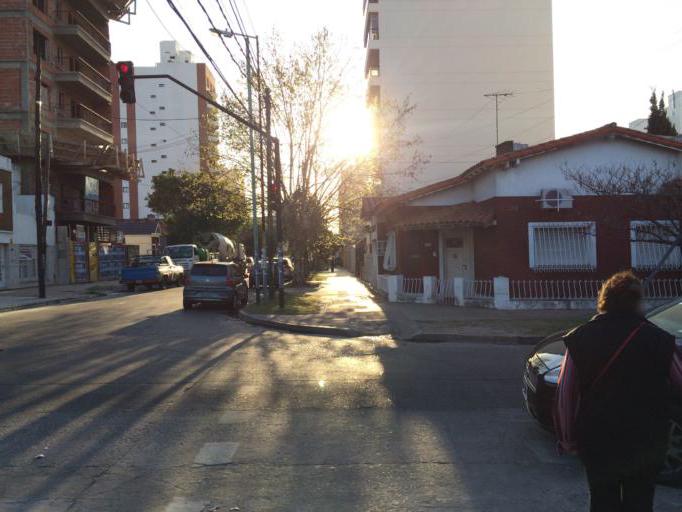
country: AR
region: Buenos Aires
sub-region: Partido de Lomas de Zamora
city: Lomas de Zamora
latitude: -34.7448
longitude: -58.3903
